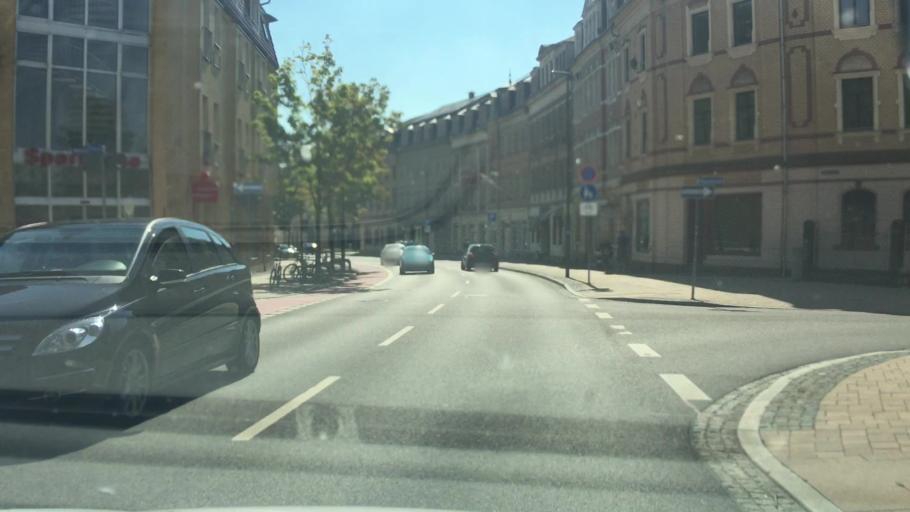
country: DE
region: Saxony
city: Pirna
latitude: 50.9708
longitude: 13.9348
